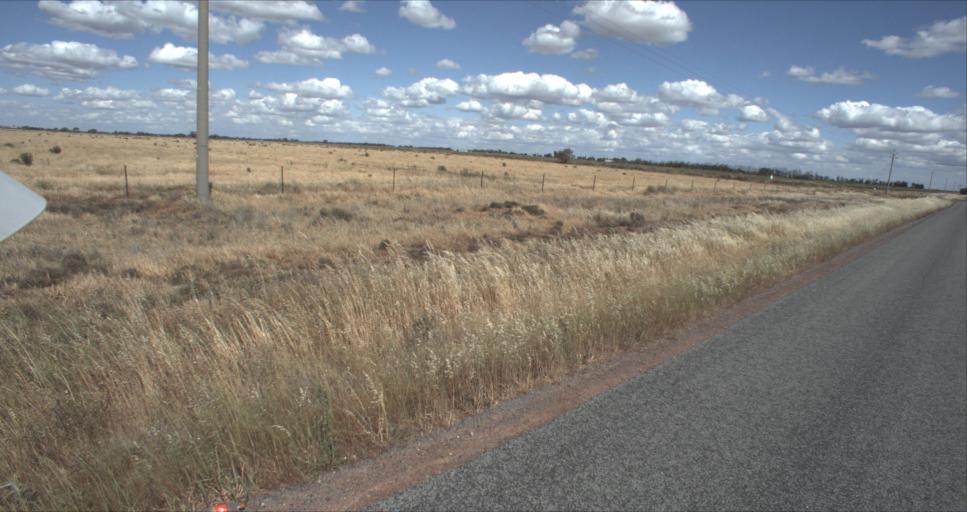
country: AU
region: New South Wales
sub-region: Leeton
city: Leeton
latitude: -34.4966
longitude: 146.2462
